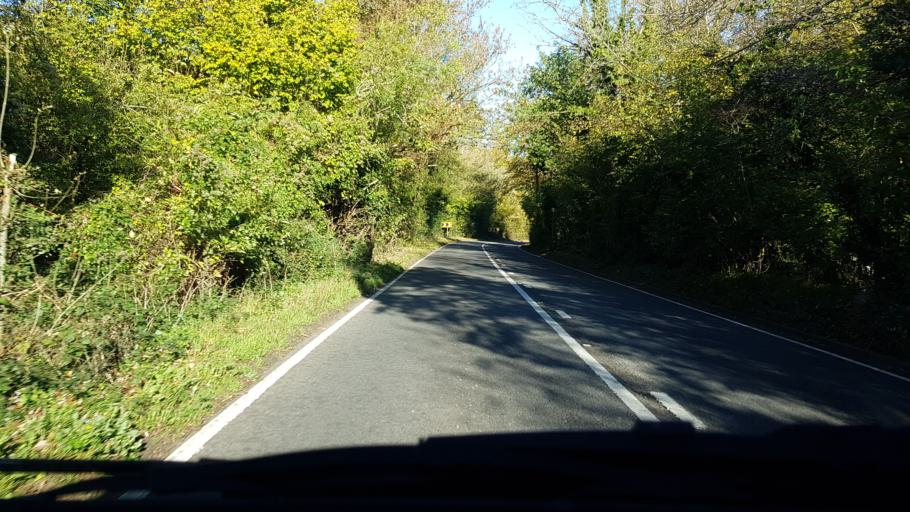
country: GB
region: England
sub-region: Surrey
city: Chilworth
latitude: 51.2417
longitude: -0.5048
